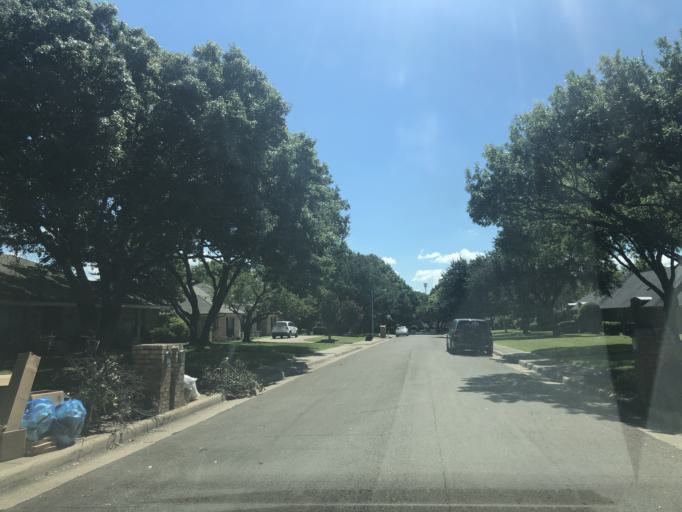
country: US
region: Texas
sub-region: Dallas County
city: Duncanville
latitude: 32.6459
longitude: -96.9309
